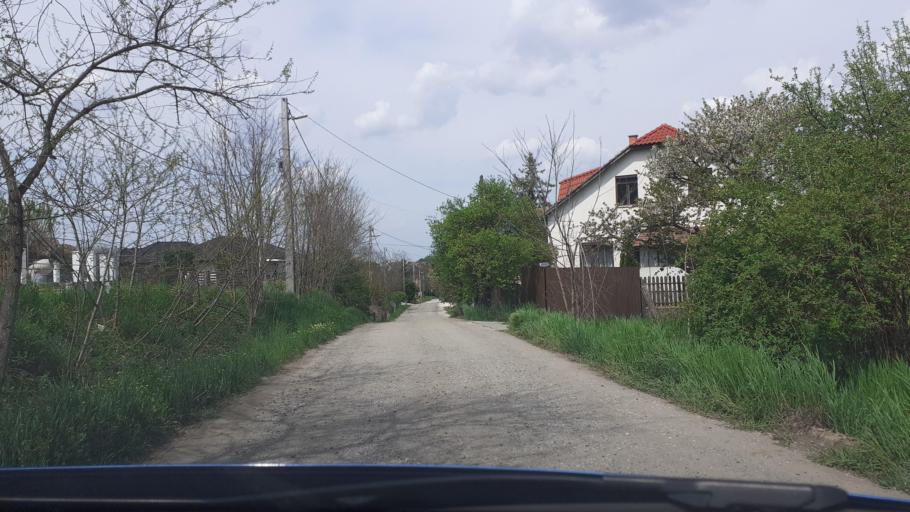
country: HU
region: Pest
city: Pecel
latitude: 47.4757
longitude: 19.3490
